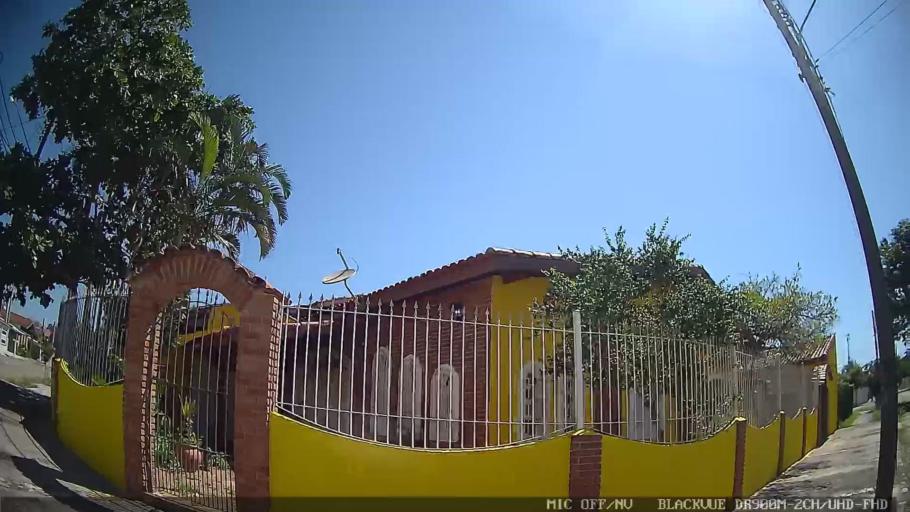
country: BR
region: Sao Paulo
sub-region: Peruibe
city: Peruibe
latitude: -24.3070
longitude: -46.9834
